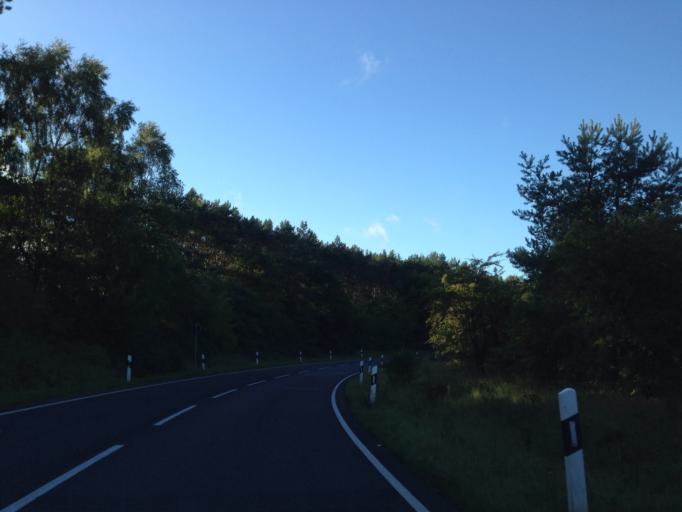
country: DE
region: Lower Saxony
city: Wendisch Evern
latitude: 53.2368
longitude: 10.4747
